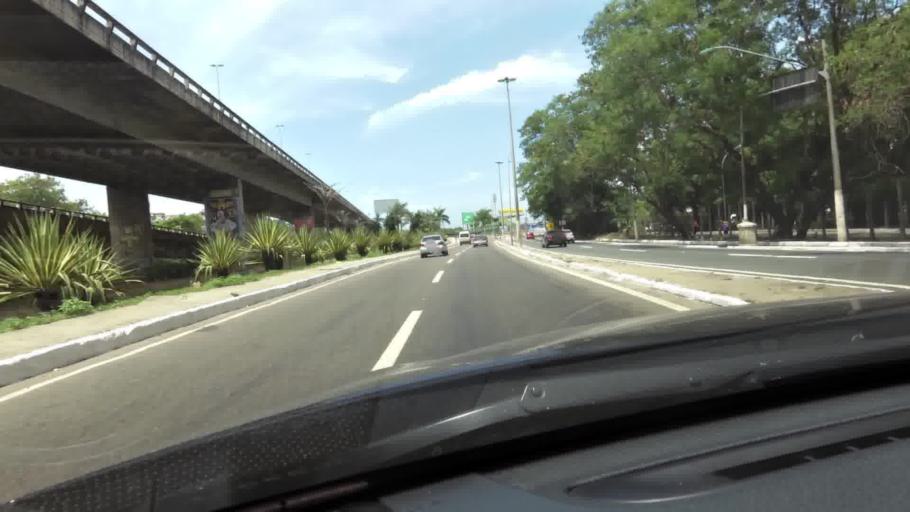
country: BR
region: Espirito Santo
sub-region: Vitoria
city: Vitoria
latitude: -20.3327
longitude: -40.3584
